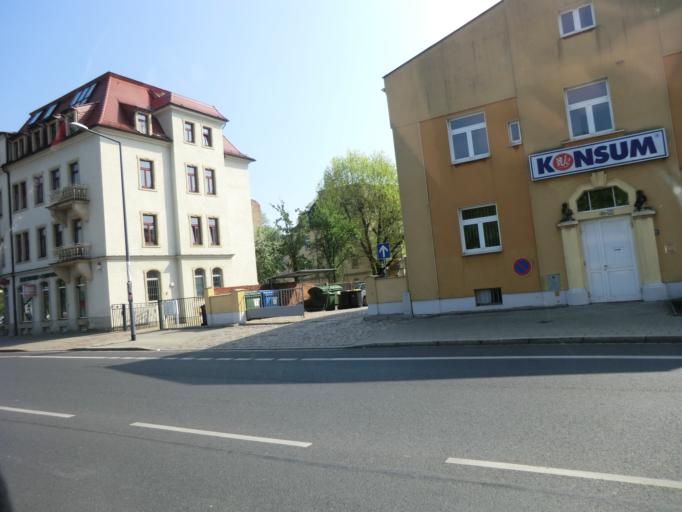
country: DE
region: Saxony
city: Dresden
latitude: 51.0321
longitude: 13.7021
